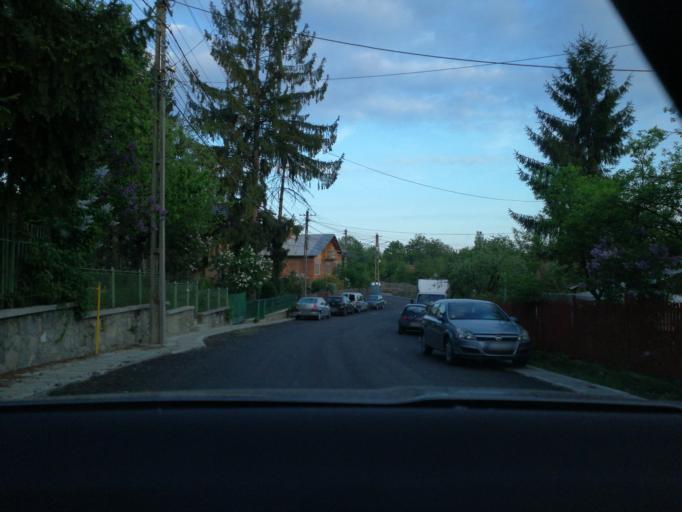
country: RO
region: Prahova
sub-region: Comuna Cornu
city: Cornu de Jos
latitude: 45.1516
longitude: 25.7011
